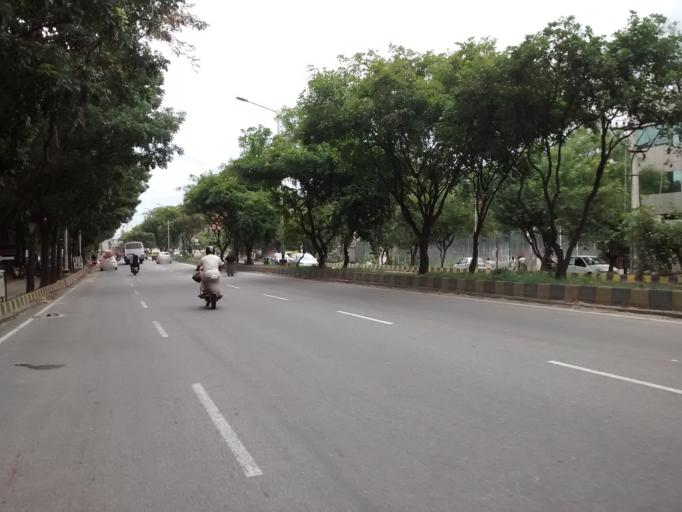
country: IN
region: Karnataka
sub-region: Bangalore Urban
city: Bangalore
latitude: 13.0338
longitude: 77.6291
